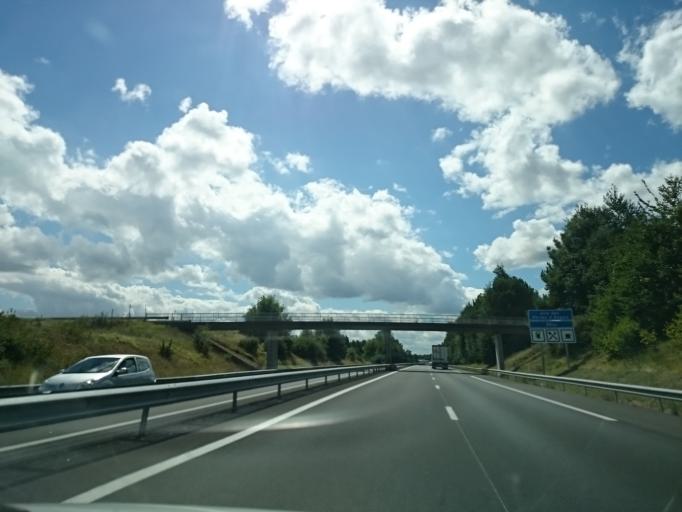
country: FR
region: Pays de la Loire
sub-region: Departement de Maine-et-Loire
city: Seiches-sur-le-Loir
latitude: 47.5949
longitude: -0.3161
